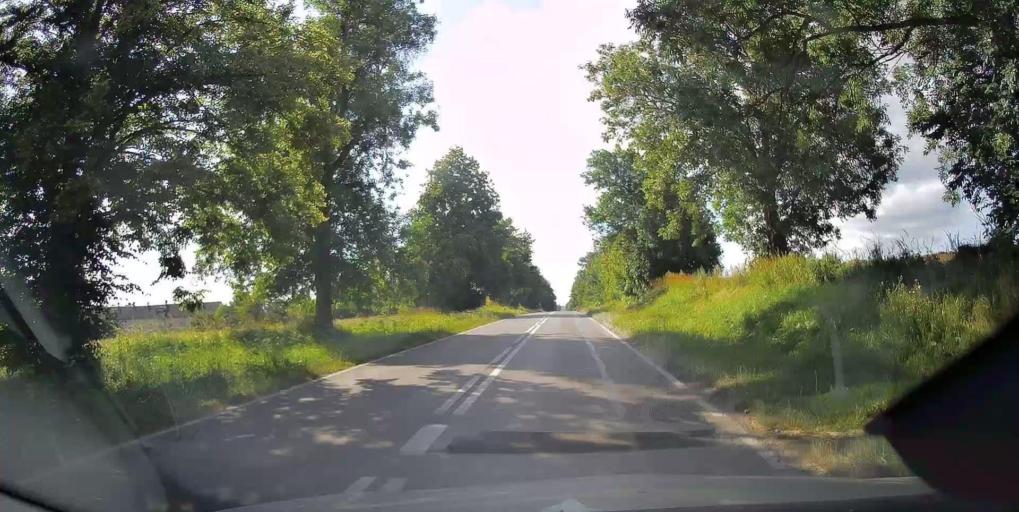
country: PL
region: Swietokrzyskie
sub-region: Powiat kielecki
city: Bodzentyn
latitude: 50.9661
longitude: 20.8921
